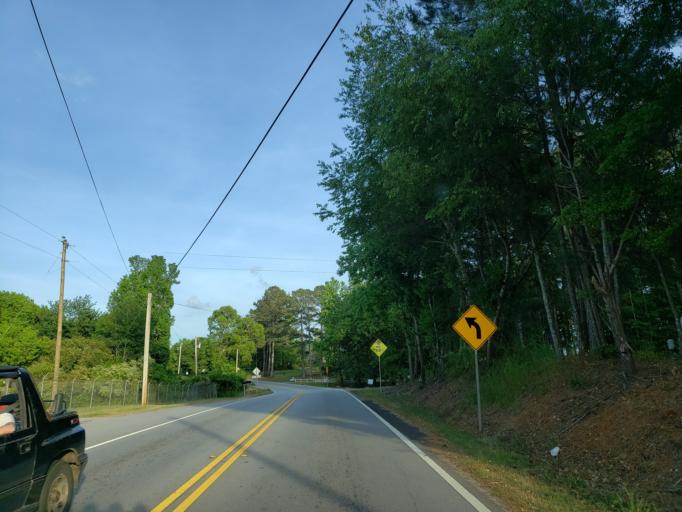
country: US
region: Georgia
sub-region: Carroll County
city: Carrollton
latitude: 33.5898
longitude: -85.1205
